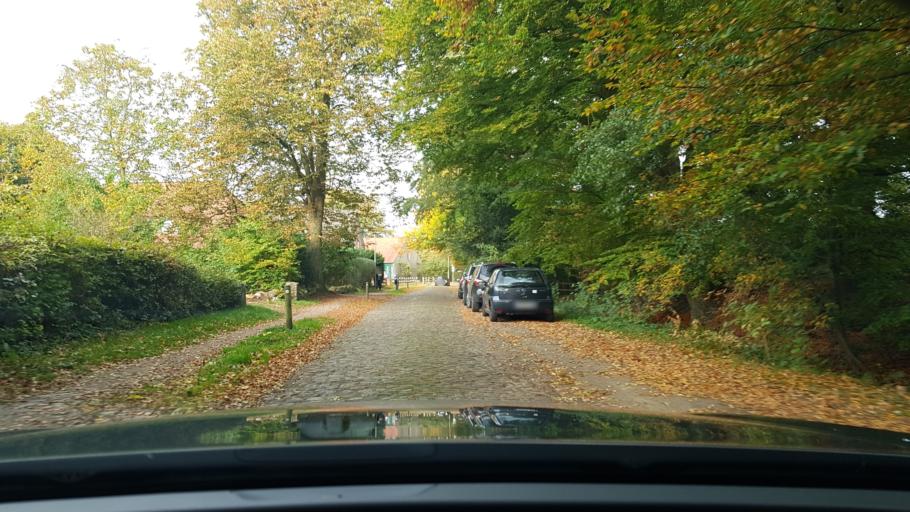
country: DE
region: Lower Saxony
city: Beverstedt
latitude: 53.4243
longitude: 8.8125
